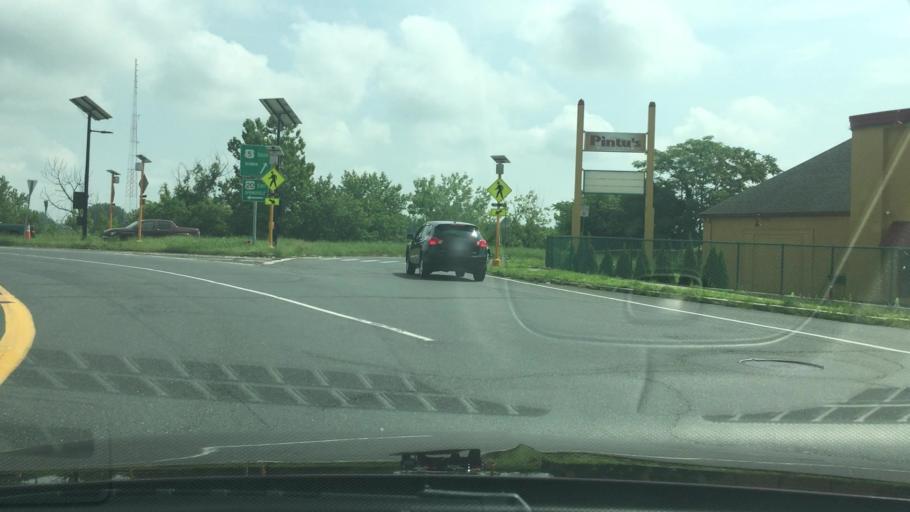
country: US
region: Massachusetts
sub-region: Hampden County
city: West Springfield
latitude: 42.1071
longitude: -72.6163
